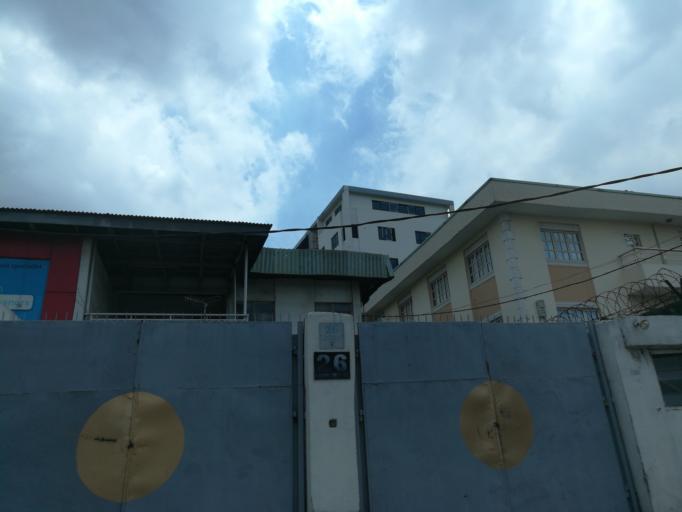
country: NG
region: Lagos
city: Ikeja
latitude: 6.6007
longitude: 3.3516
